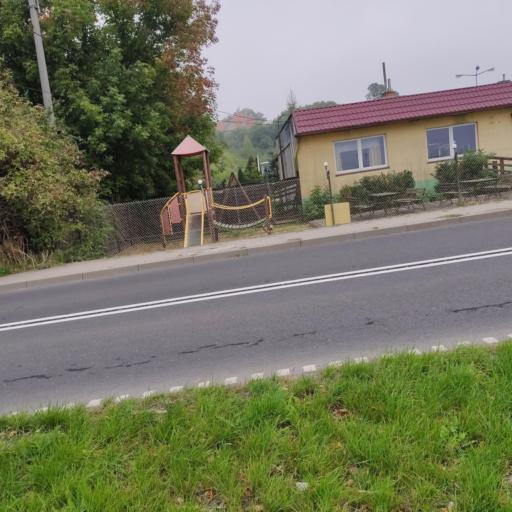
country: PL
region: Kujawsko-Pomorskie
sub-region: Powiat zninski
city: Znin
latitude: 52.8551
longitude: 17.7519
